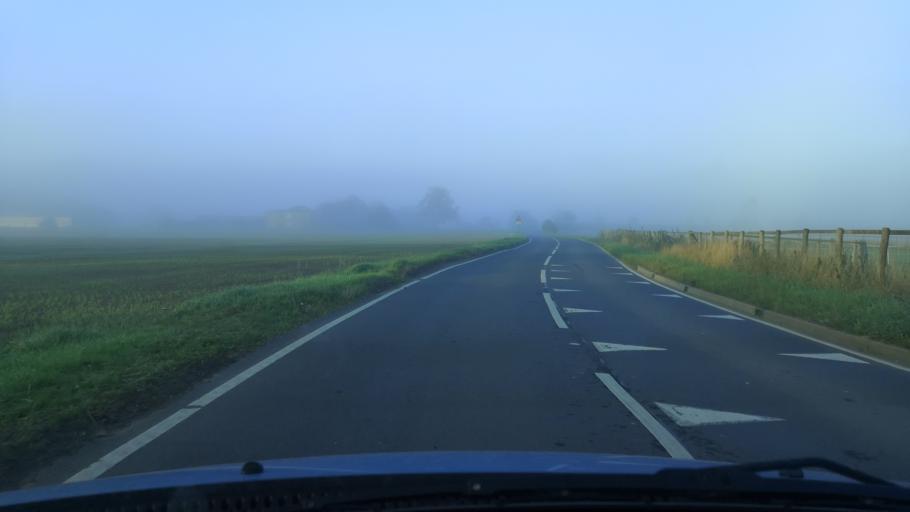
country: GB
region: England
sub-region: North Lincolnshire
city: Eastoft
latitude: 53.6330
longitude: -0.7901
